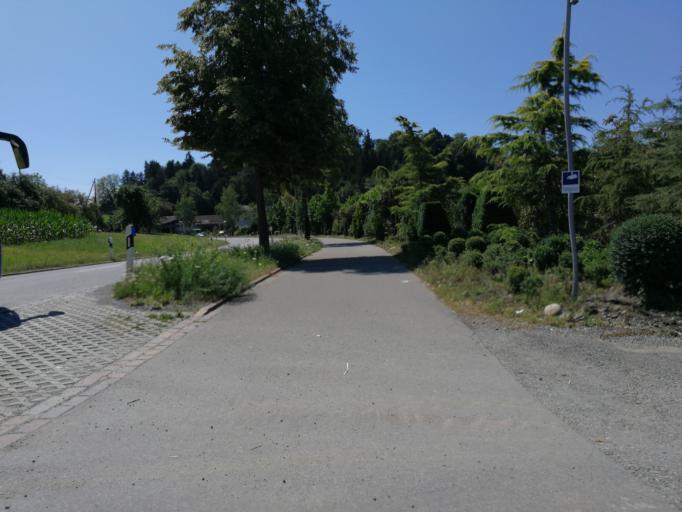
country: CH
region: Zurich
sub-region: Bezirk Uster
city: Uster / Nossikon
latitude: 47.3331
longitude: 8.7413
